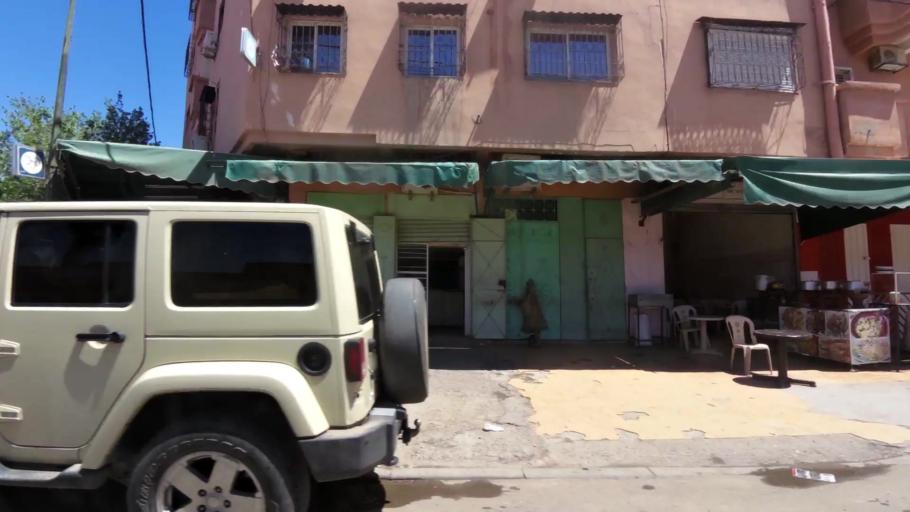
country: MA
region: Marrakech-Tensift-Al Haouz
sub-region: Marrakech
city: Marrakesh
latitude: 31.6276
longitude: -8.0189
